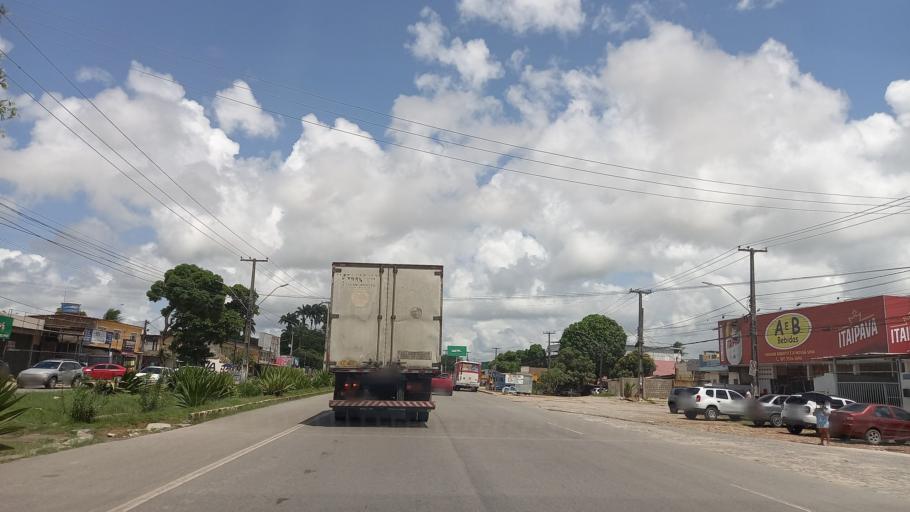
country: BR
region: Pernambuco
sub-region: Jaboatao Dos Guararapes
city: Jaboatao
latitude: -8.2338
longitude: -34.9785
